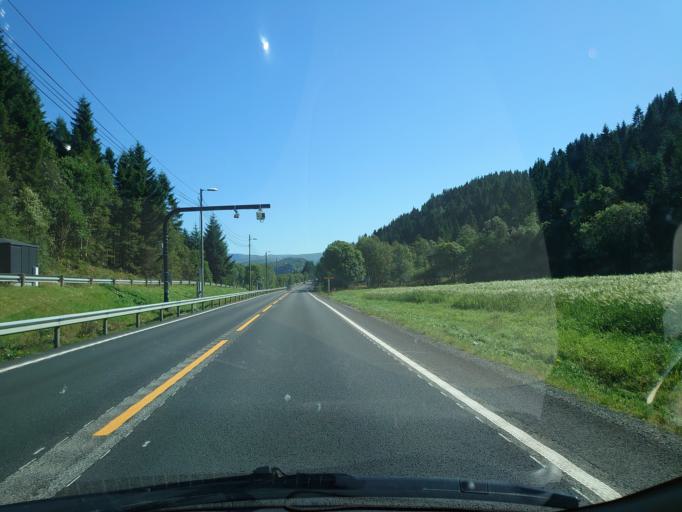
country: NO
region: Hordaland
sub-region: Bergen
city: Hylkje
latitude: 60.4704
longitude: 5.3683
